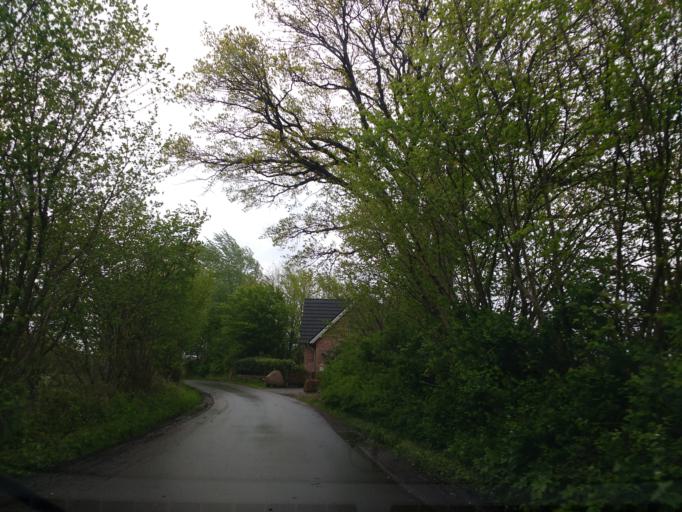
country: DE
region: Schleswig-Holstein
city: Waabs
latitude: 54.5170
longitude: 9.9709
